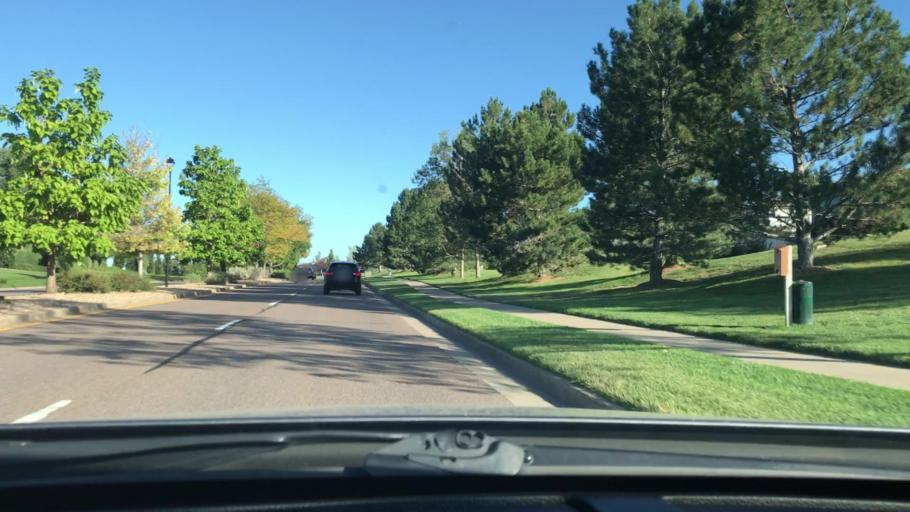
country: US
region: Colorado
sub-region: Arapahoe County
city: Dove Valley
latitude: 39.6079
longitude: -104.7685
